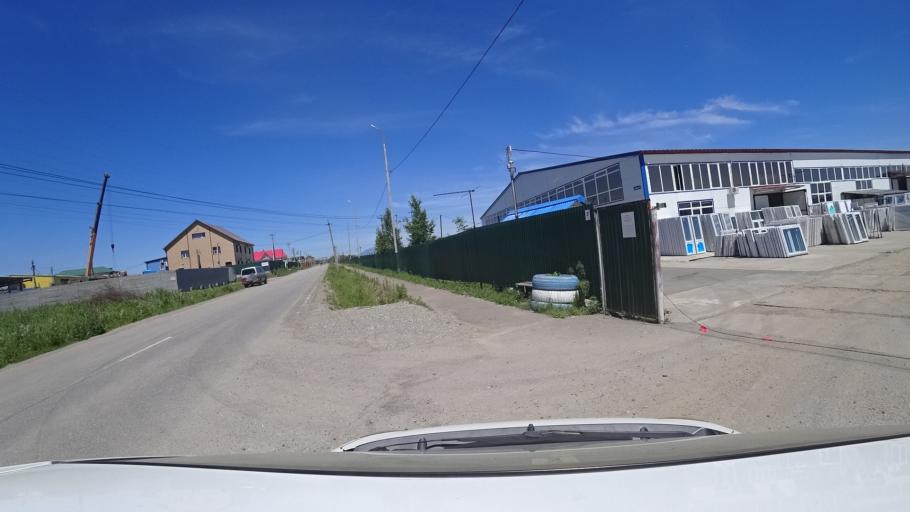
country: RU
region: Khabarovsk Krai
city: Topolevo
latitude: 48.4996
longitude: 135.1838
